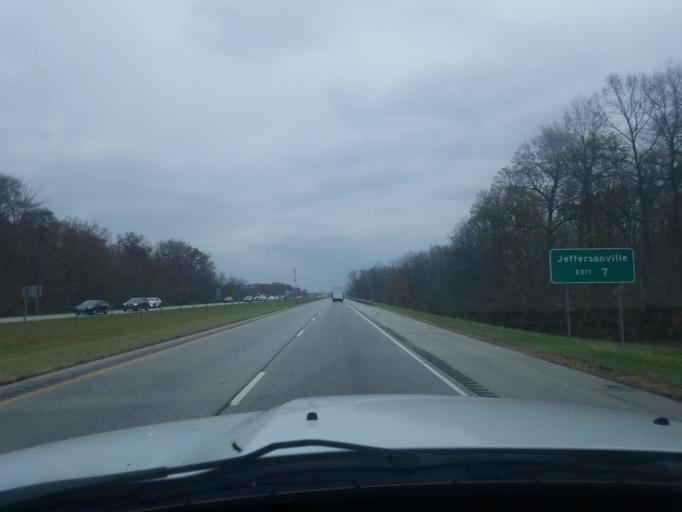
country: US
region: Indiana
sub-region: Clark County
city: Clarksville
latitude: 38.3451
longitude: -85.7719
